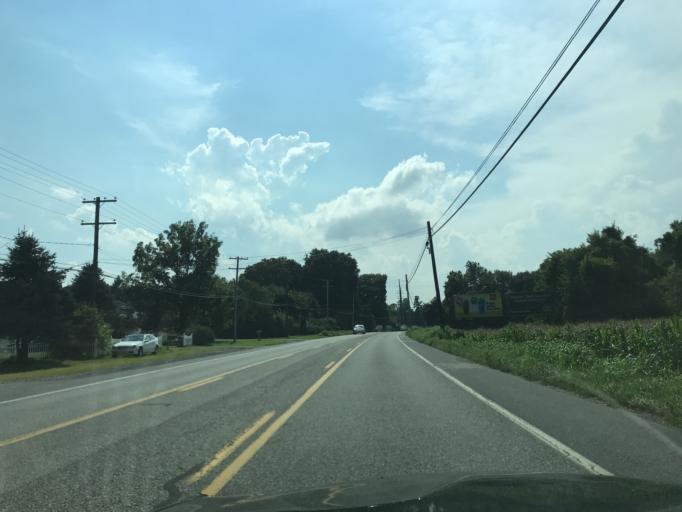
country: US
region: Pennsylvania
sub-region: Lancaster County
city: Mountville
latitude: 40.0326
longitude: -76.4655
